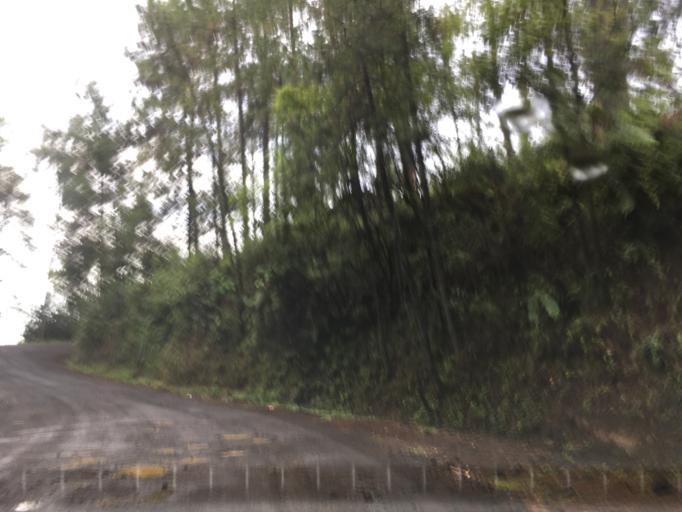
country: MX
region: Michoacan
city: Nuevo San Juan Parangaricutiro
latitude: 19.4468
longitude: -102.1772
